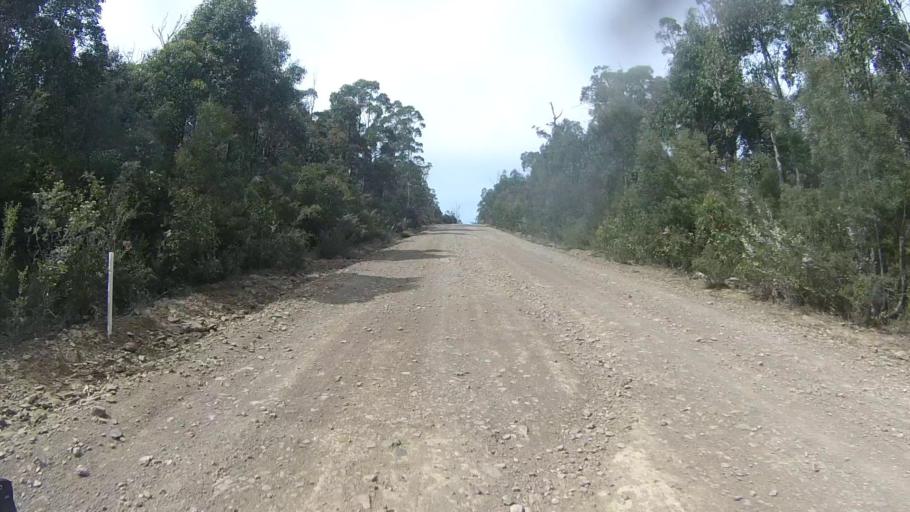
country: AU
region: Tasmania
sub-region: Sorell
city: Sorell
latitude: -42.7562
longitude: 147.8296
